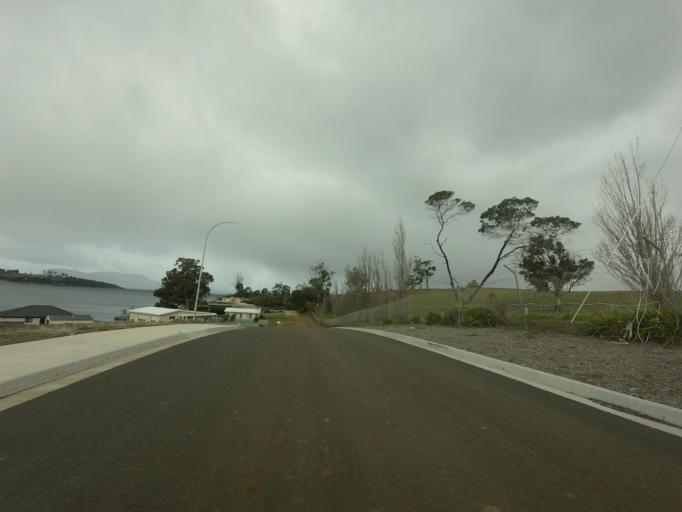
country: AU
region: Tasmania
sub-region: Sorell
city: Sorell
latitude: -42.5430
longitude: 147.9137
